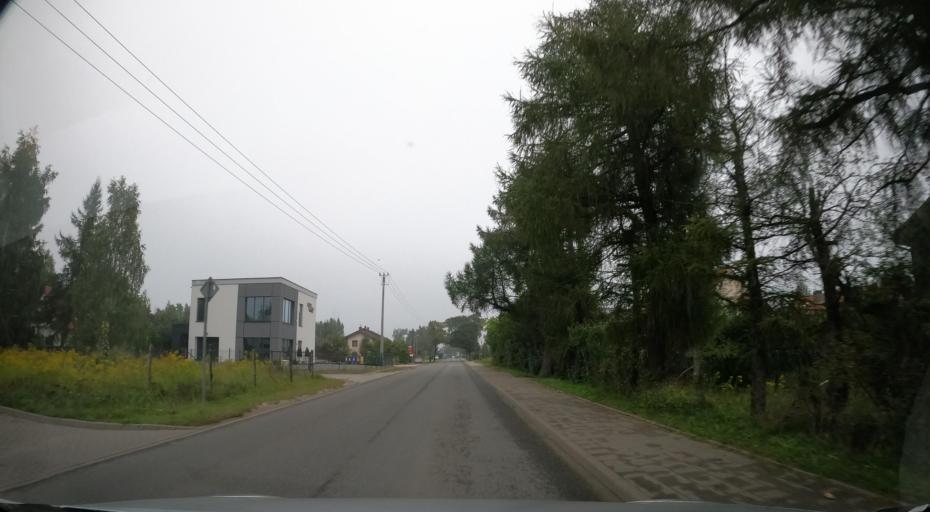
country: PL
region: Pomeranian Voivodeship
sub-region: Powiat kartuski
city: Chwaszczyno
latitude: 54.4248
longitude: 18.4575
